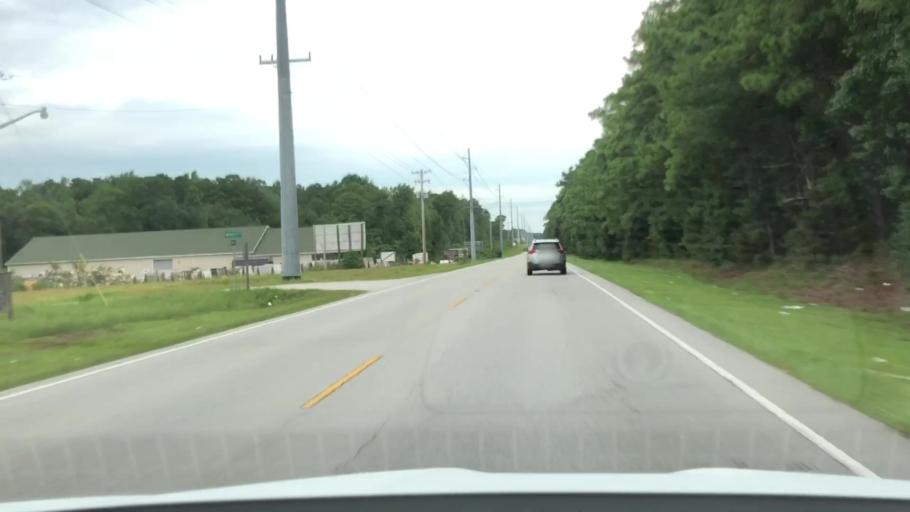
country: US
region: North Carolina
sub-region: Carteret County
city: Cape Carteret
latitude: 34.7315
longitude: -77.0792
